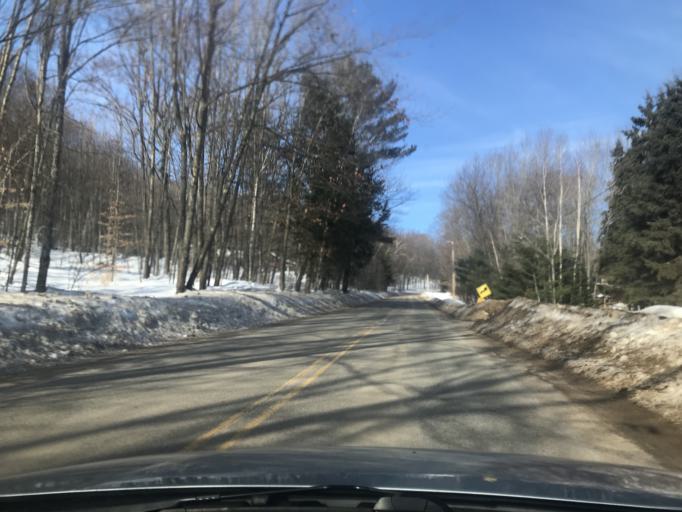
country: US
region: Michigan
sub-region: Dickinson County
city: Kingsford
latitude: 45.4030
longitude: -88.3450
